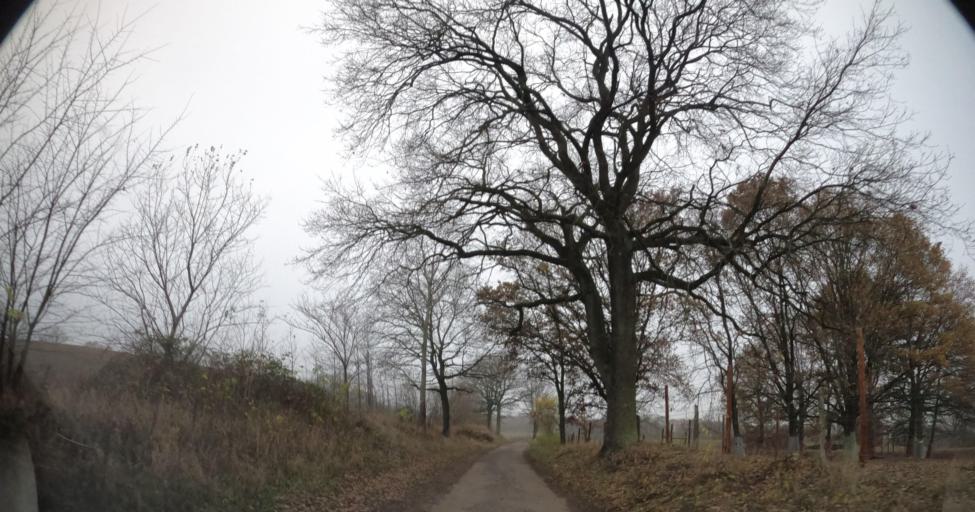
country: PL
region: West Pomeranian Voivodeship
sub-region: Powiat drawski
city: Drawsko Pomorskie
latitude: 53.5761
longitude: 15.8217
